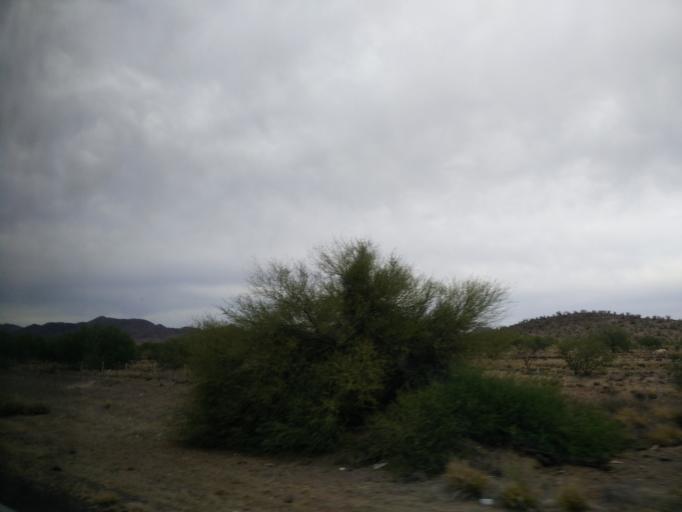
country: MX
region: Sonora
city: Hermosillo
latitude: 28.9190
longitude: -110.9522
